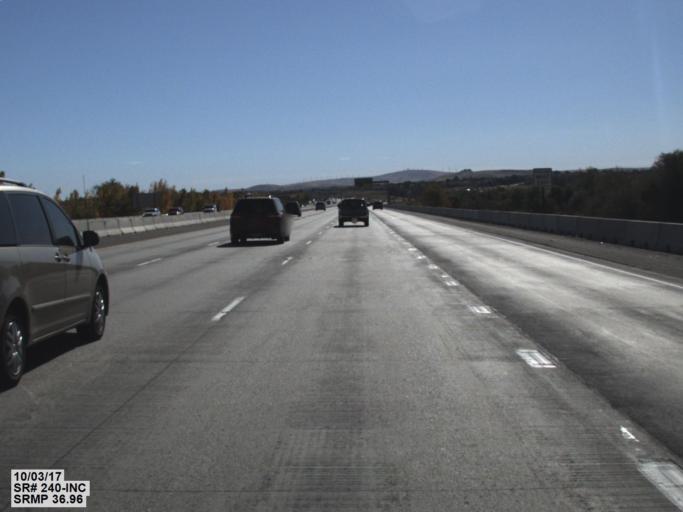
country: US
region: Washington
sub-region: Benton County
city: Richland
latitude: 46.2483
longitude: -119.2530
